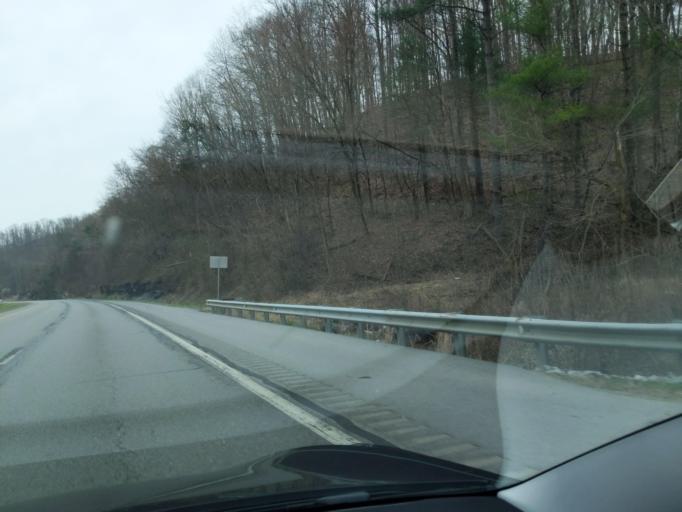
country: US
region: Kentucky
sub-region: Knox County
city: Barbourville
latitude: 36.8710
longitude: -83.8108
